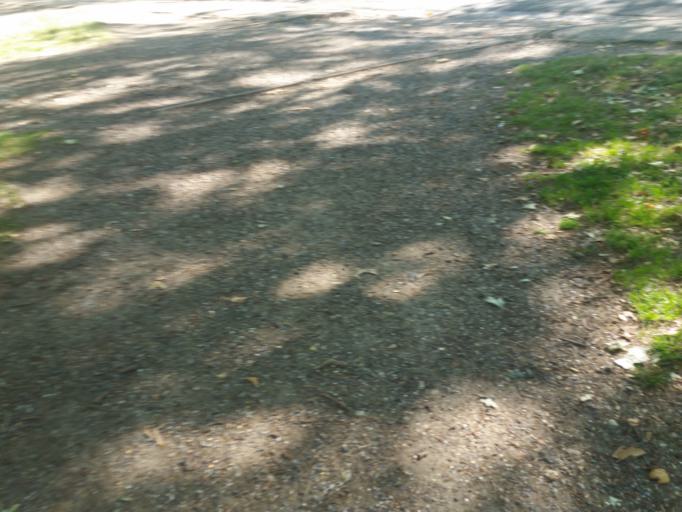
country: GB
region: England
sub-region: Greater London
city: Harringay
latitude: 51.5724
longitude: -0.0978
